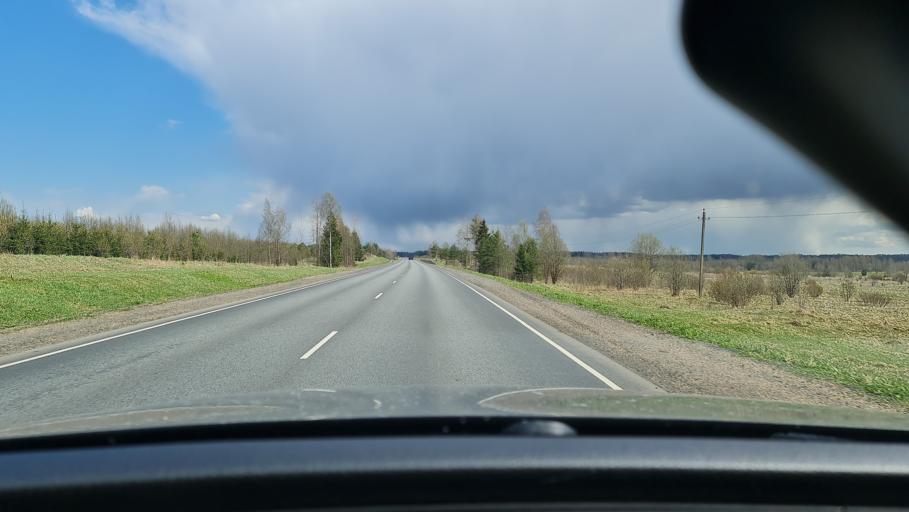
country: RU
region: Tverskaya
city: Zapadnaya Dvina
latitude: 56.3029
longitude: 32.3982
